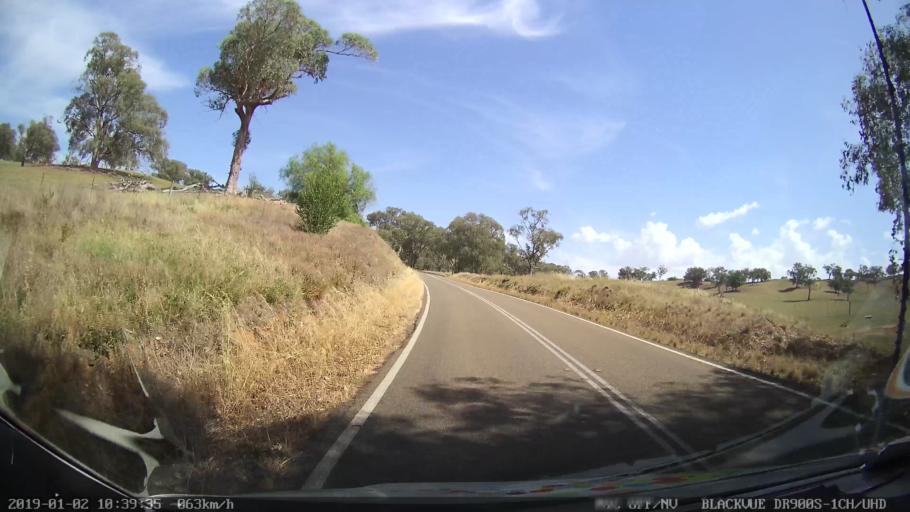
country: AU
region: New South Wales
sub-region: Gundagai
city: Gundagai
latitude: -34.8094
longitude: 148.3188
